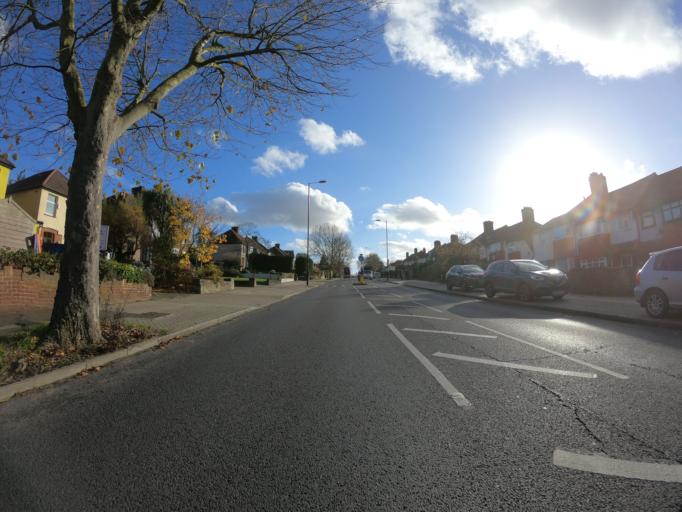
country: GB
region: England
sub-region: Greater London
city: Blackheath
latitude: 51.4396
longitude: 0.0169
